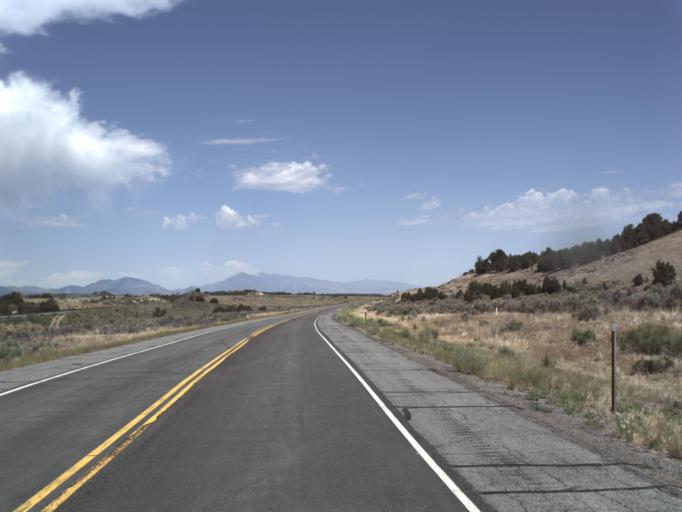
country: US
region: Utah
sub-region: Utah County
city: Genola
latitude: 39.9688
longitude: -112.2549
